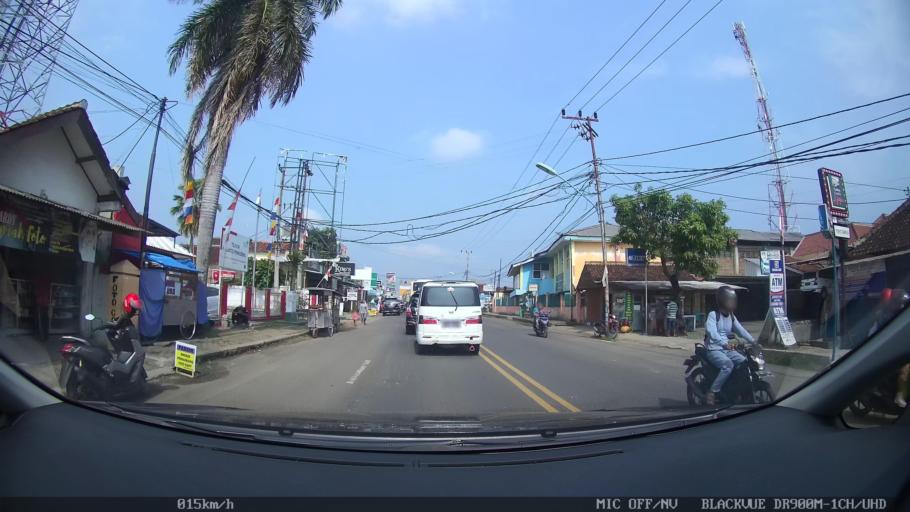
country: ID
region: Lampung
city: Gedongtataan
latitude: -5.3799
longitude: 105.0997
